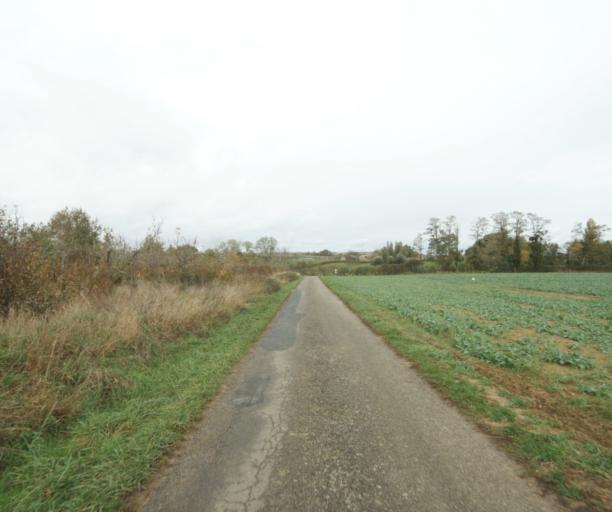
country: FR
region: Rhone-Alpes
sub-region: Departement de l'Ain
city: Pont-de-Vaux
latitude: 46.4587
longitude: 4.8807
